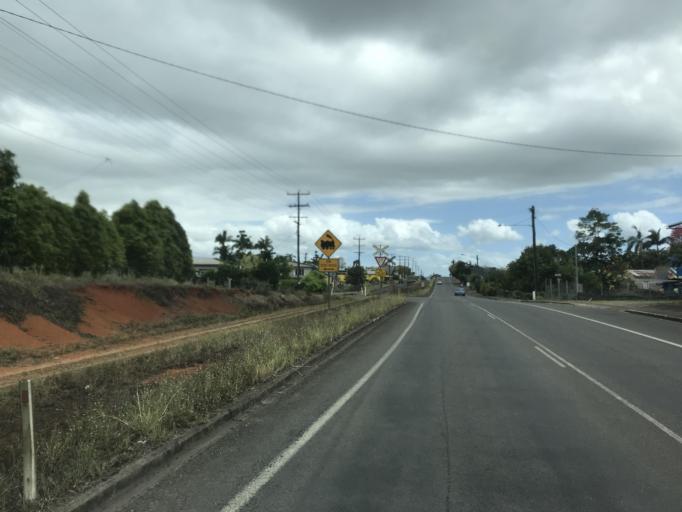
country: AU
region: Queensland
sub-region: Cassowary Coast
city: Innisfail
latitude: -17.5983
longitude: 145.9948
